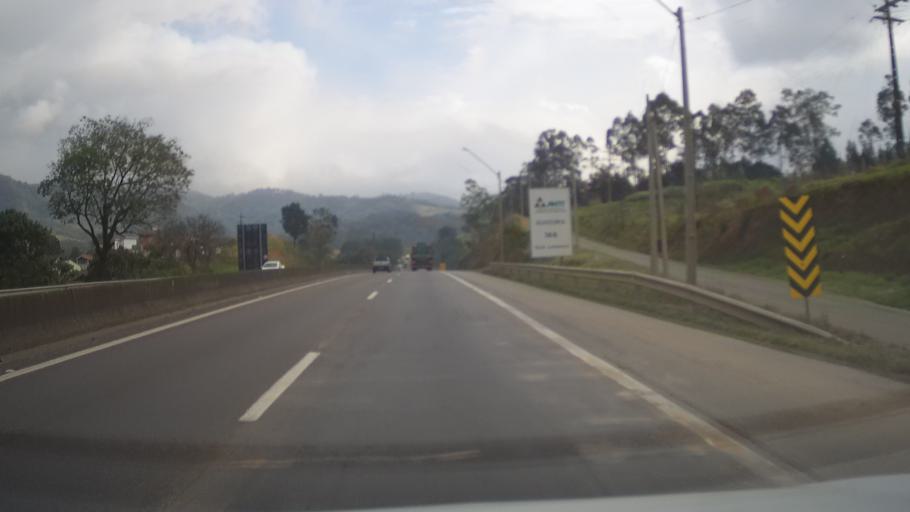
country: BR
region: Minas Gerais
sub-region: Extrema
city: Extrema
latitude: -22.8907
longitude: -46.4133
